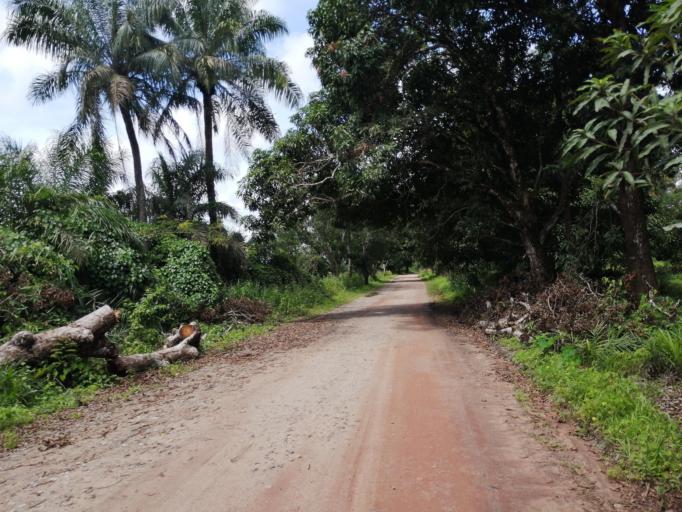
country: SL
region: Northern Province
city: Pepel
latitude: 8.6651
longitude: -13.0018
